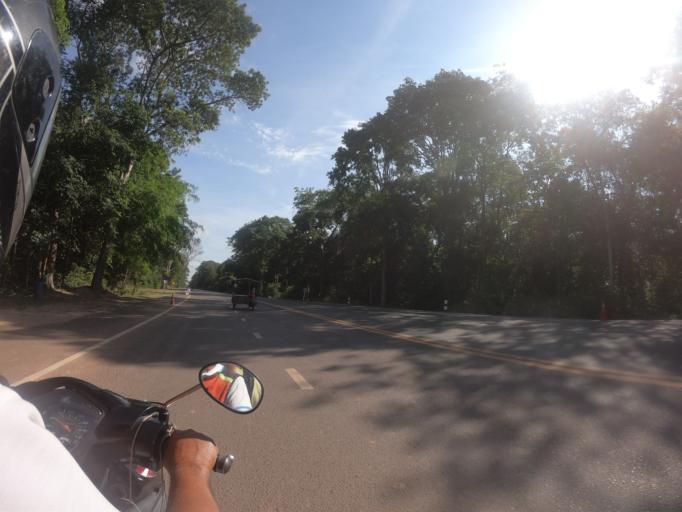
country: TH
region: Surin
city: Kap Choeng
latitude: 14.4369
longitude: 103.7007
